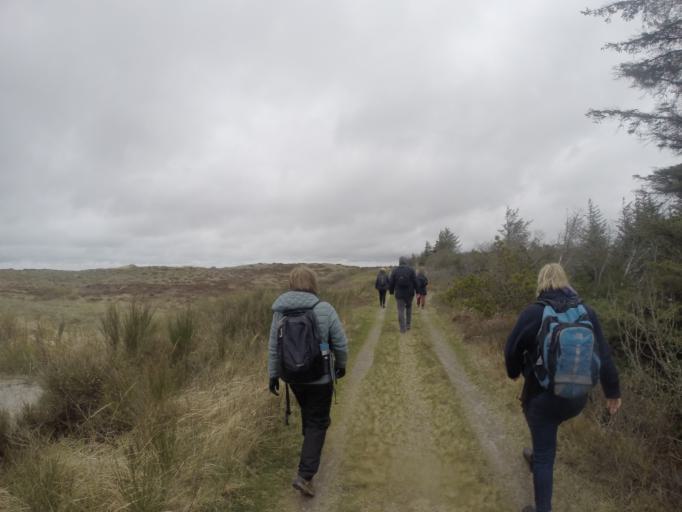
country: DK
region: North Denmark
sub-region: Thisted Kommune
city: Hurup
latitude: 56.9022
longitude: 8.3410
